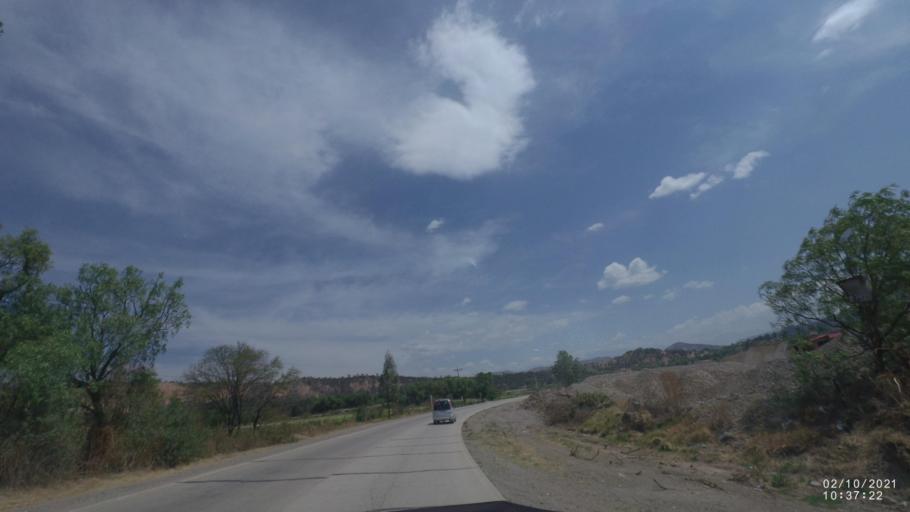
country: BO
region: Cochabamba
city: Capinota
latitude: -17.6445
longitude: -66.2641
